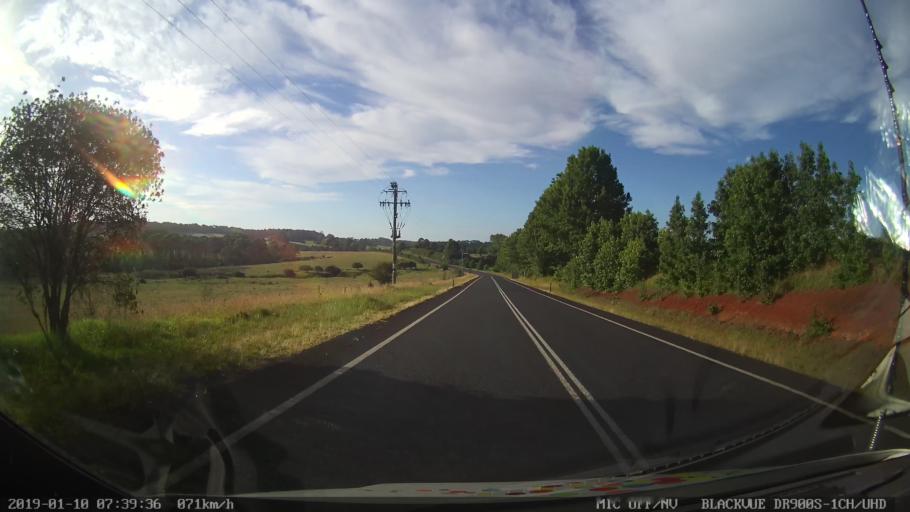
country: AU
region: New South Wales
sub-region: Bellingen
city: Dorrigo
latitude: -30.3588
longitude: 152.7197
